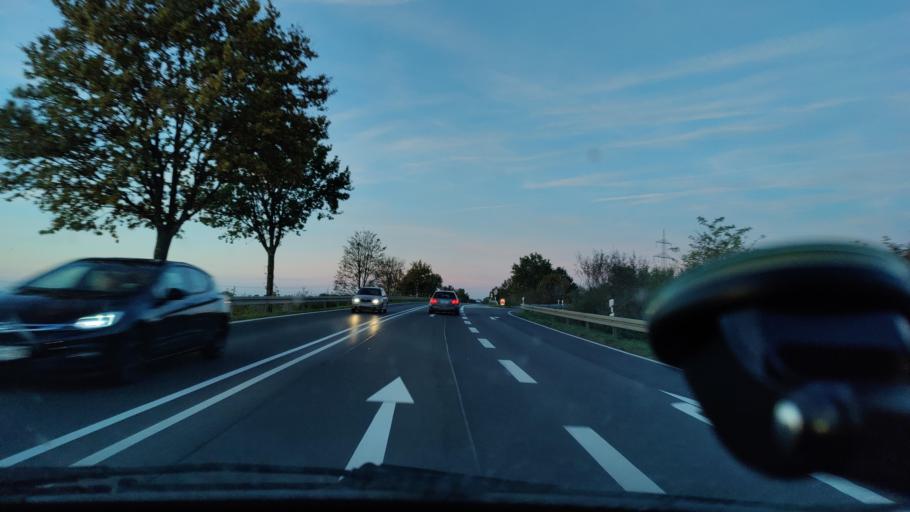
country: DE
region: North Rhine-Westphalia
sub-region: Regierungsbezirk Koln
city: Heinsberg
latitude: 51.0422
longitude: 6.0994
